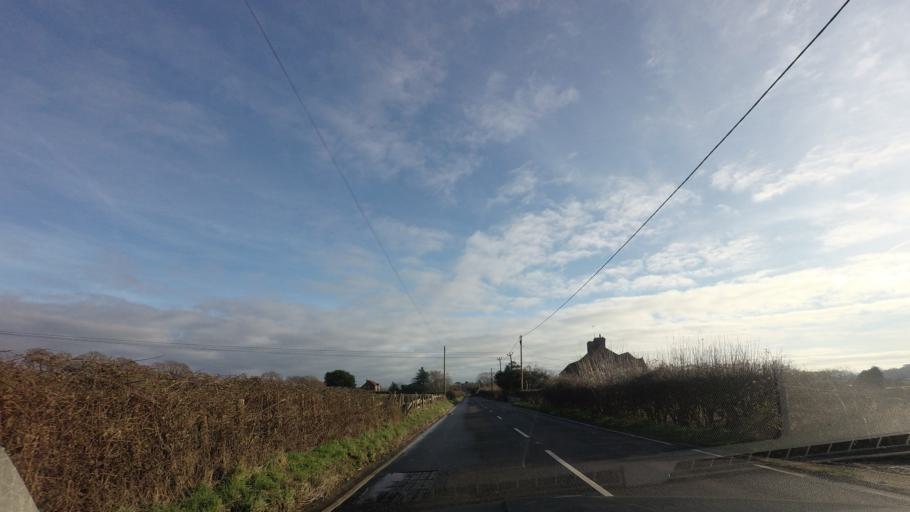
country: GB
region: England
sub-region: East Sussex
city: Bexhill-on-Sea
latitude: 50.8720
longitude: 0.4378
